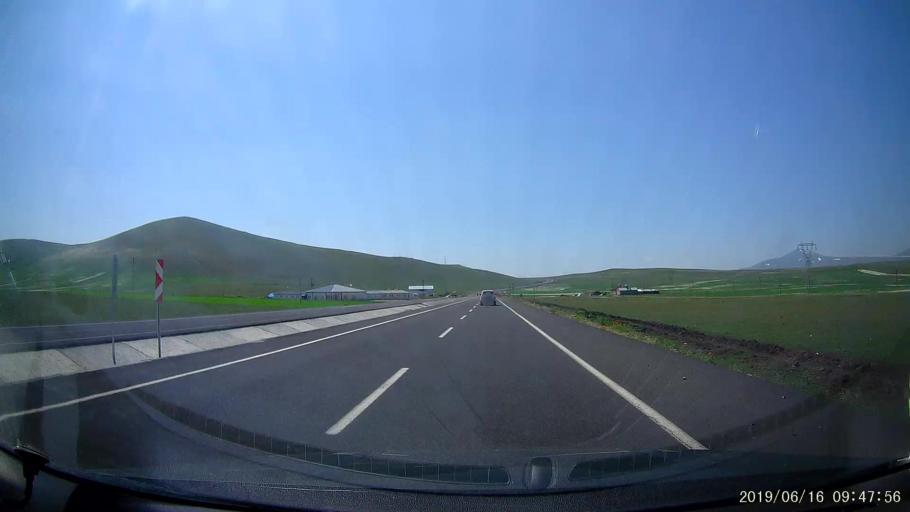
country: TR
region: Kars
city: Digor
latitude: 40.4391
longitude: 43.3494
